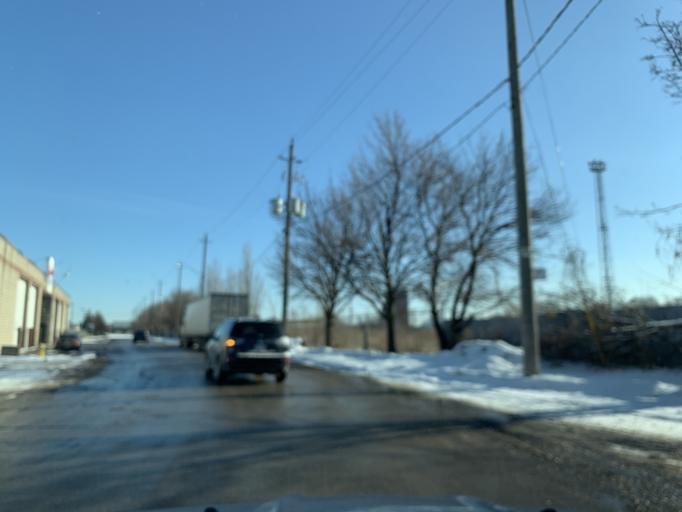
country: CA
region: Ontario
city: Toronto
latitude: 43.6687
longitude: -79.4755
